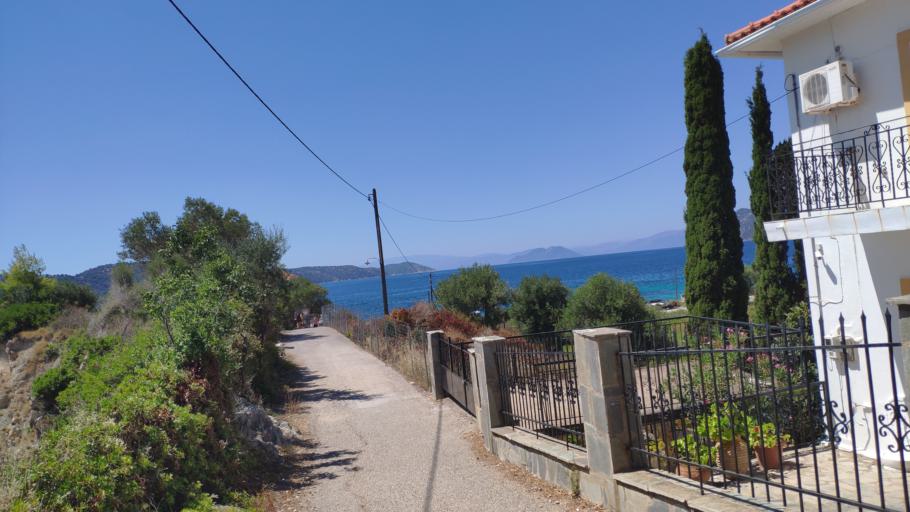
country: GR
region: West Greece
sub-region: Nomos Aitolias kai Akarnanias
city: Kandila
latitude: 38.6163
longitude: 20.9278
